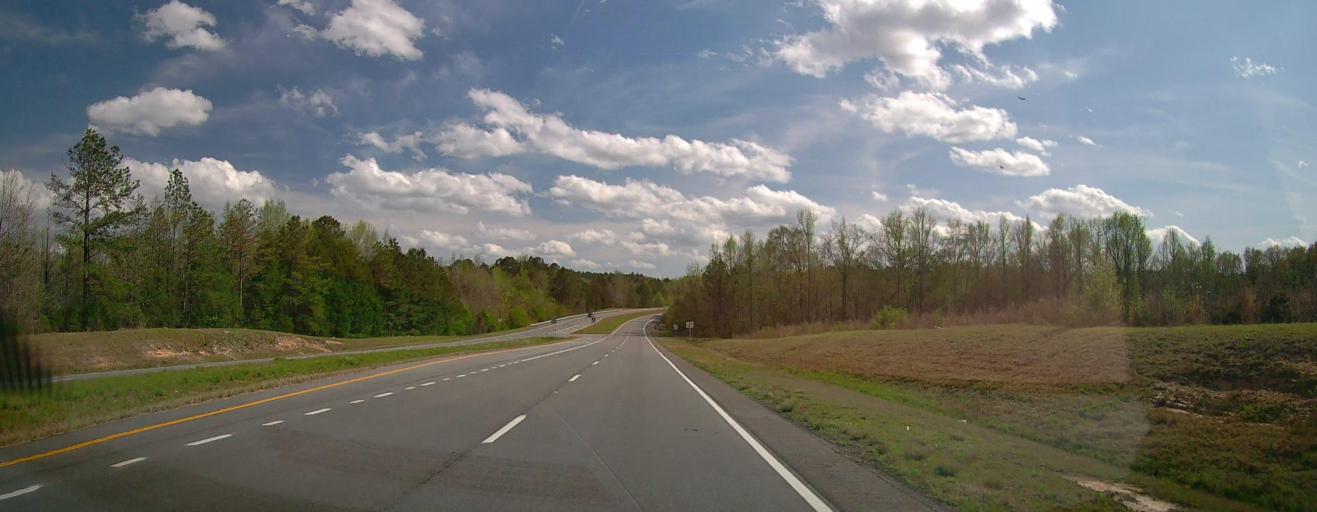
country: US
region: Georgia
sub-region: Baldwin County
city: Hardwick
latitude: 32.9887
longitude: -83.2126
